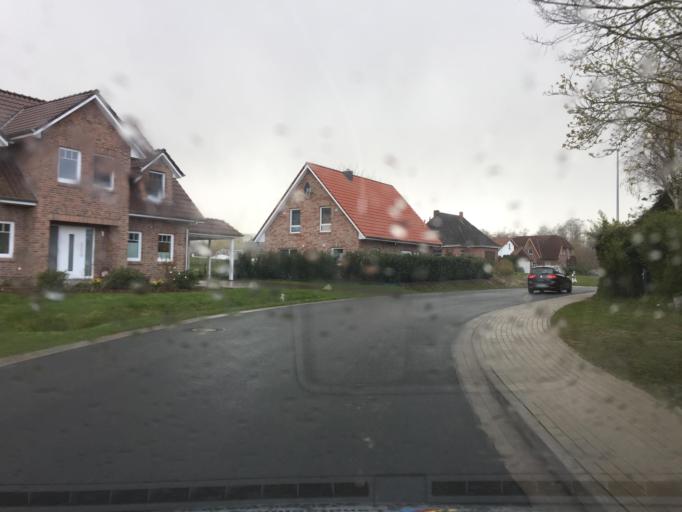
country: DE
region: Lower Saxony
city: Syke
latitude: 52.9344
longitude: 8.8876
